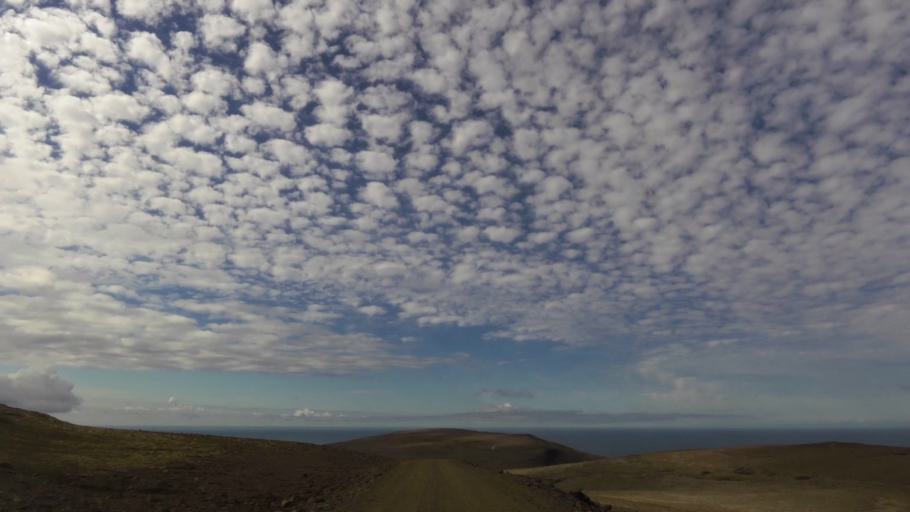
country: IS
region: West
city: Olafsvik
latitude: 65.6214
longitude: -24.2790
